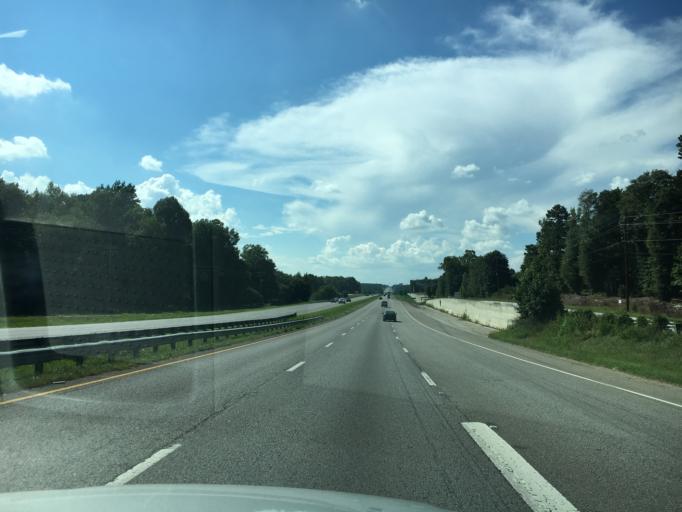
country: US
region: South Carolina
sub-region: Greenville County
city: Fountain Inn
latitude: 34.6699
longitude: -82.1849
